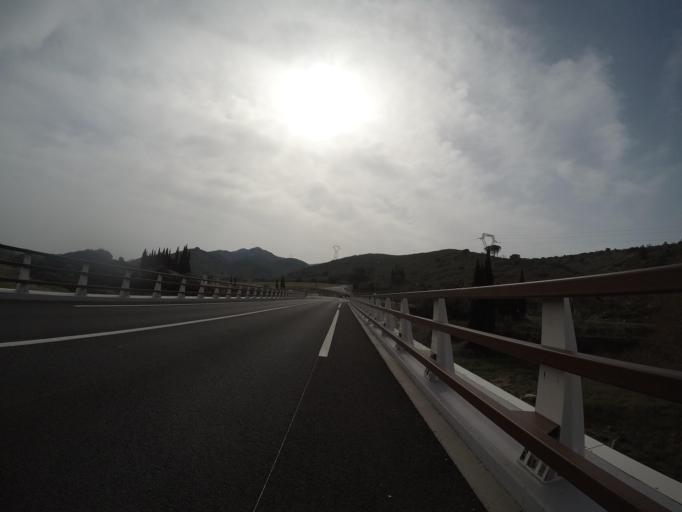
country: FR
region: Languedoc-Roussillon
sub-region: Departement des Pyrenees-Orientales
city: Estagel
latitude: 42.7761
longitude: 2.7087
